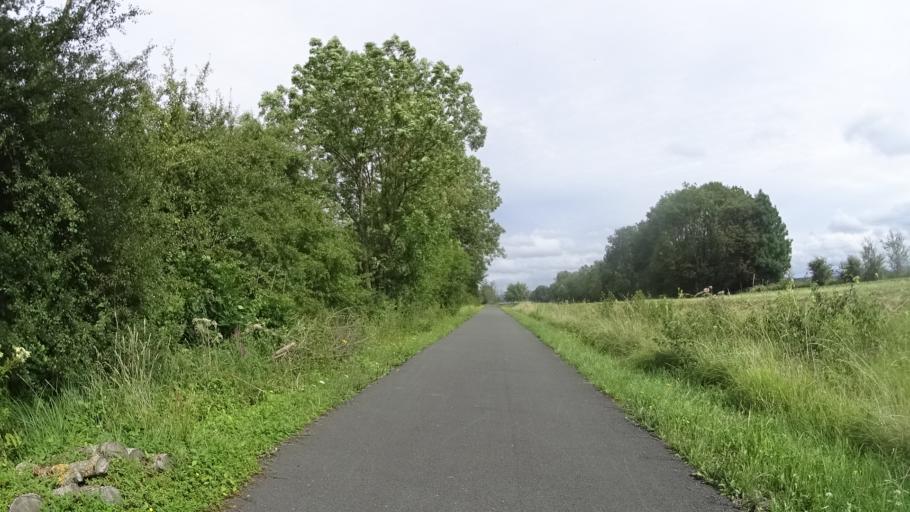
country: FR
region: Lorraine
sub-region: Departement de la Moselle
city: Sarrebourg
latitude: 48.6944
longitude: 7.0323
